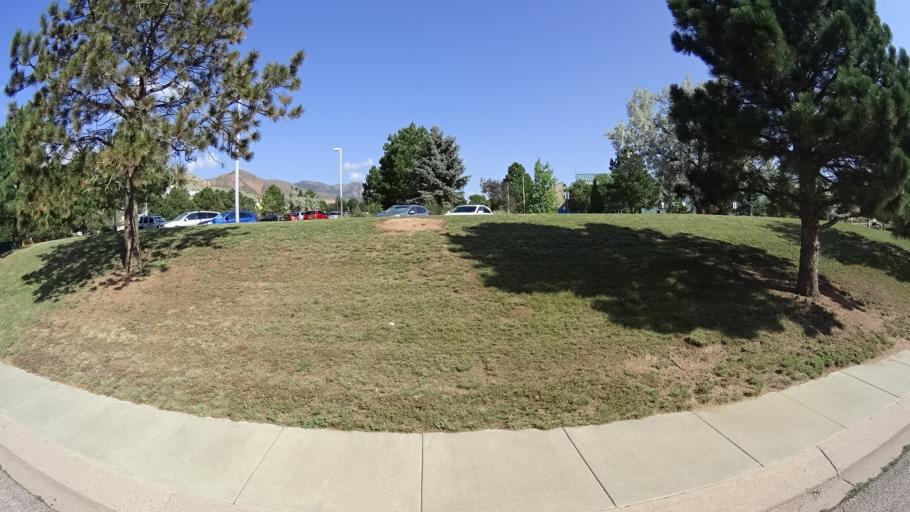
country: US
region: Colorado
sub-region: El Paso County
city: Manitou Springs
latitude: 38.9062
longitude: -104.8714
